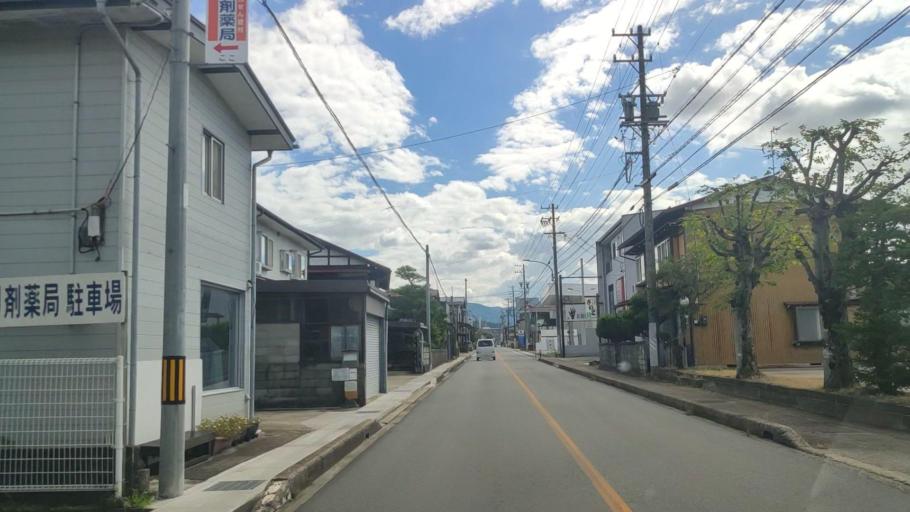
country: JP
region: Gifu
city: Takayama
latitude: 36.1584
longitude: 137.2529
